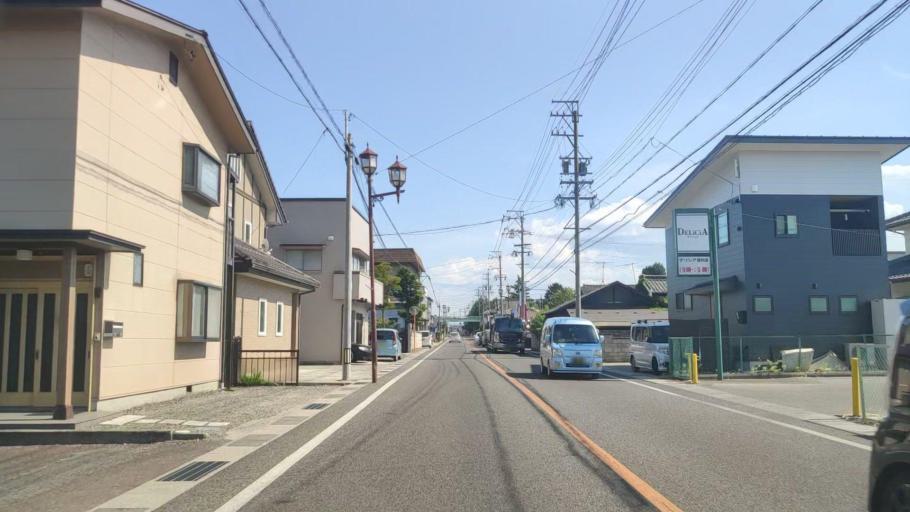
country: JP
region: Nagano
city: Toyoshina
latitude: 36.2967
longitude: 137.9056
